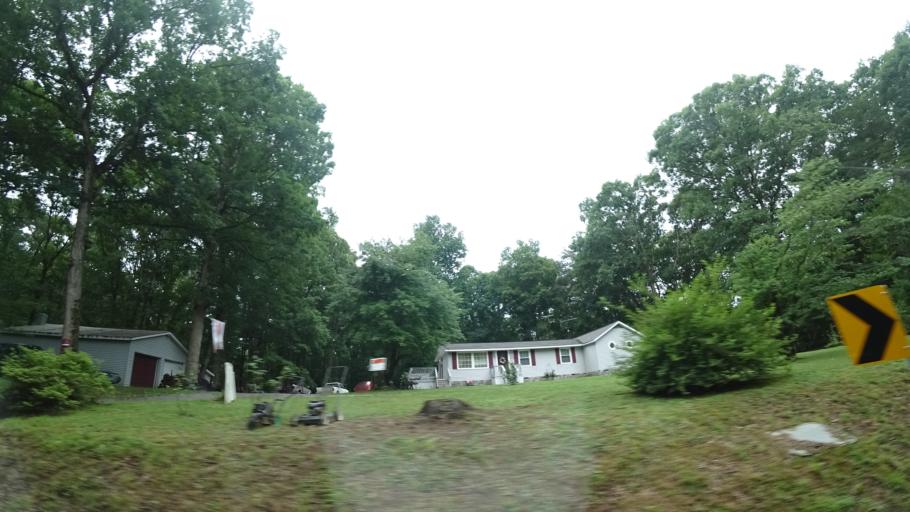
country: US
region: Virginia
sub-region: Spotsylvania County
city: Spotsylvania
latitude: 38.1332
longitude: -77.7887
